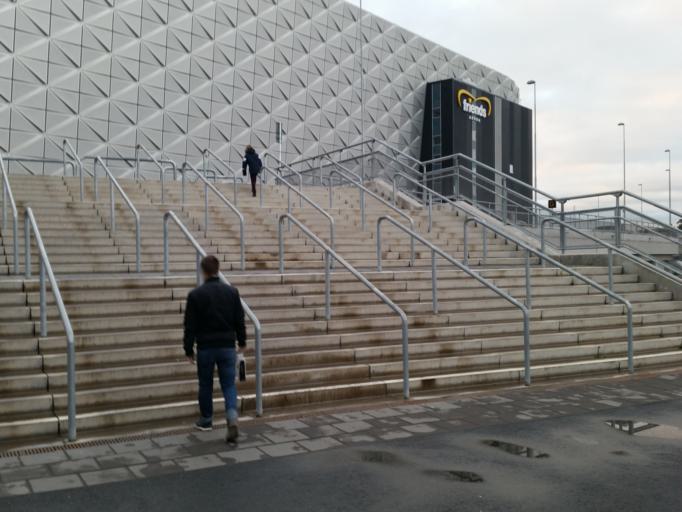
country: SE
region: Stockholm
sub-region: Solna Kommun
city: Solna
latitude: 59.3727
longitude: 18.0029
